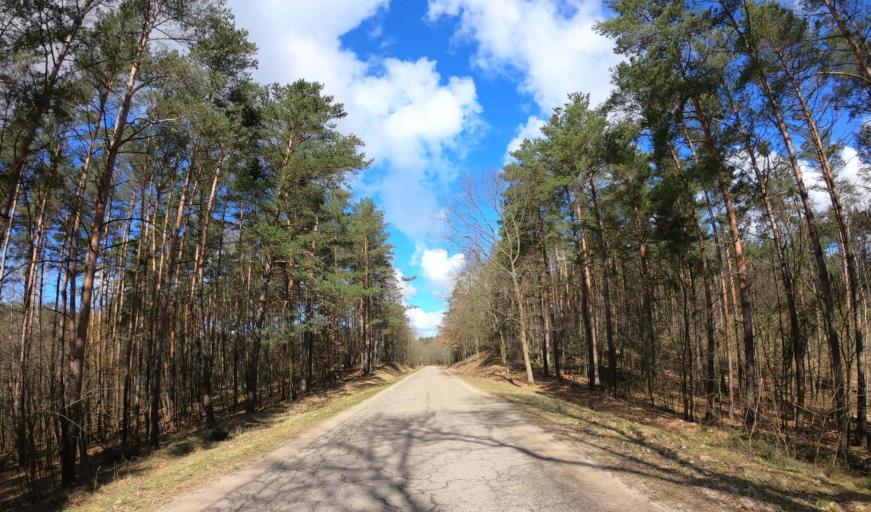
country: PL
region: West Pomeranian Voivodeship
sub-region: Powiat drawski
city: Zlocieniec
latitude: 53.4740
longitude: 15.9260
